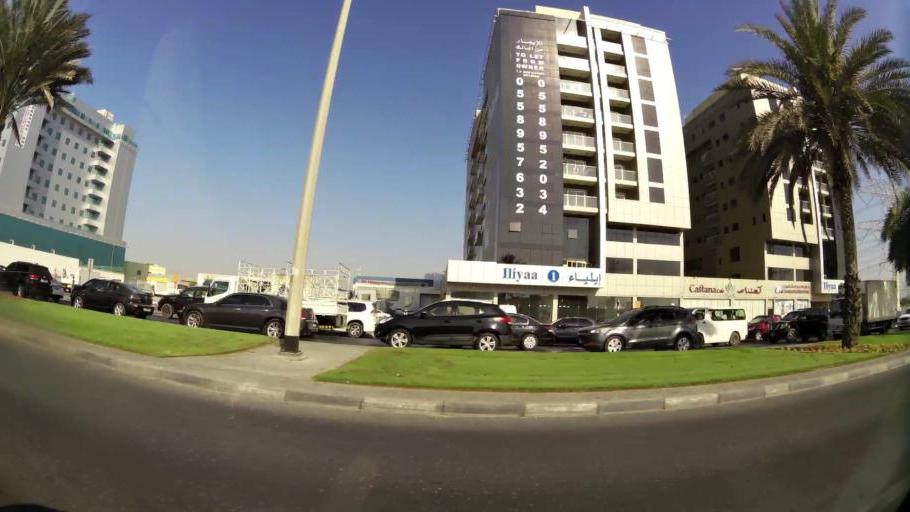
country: AE
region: Ash Shariqah
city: Sharjah
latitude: 25.2971
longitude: 55.3965
